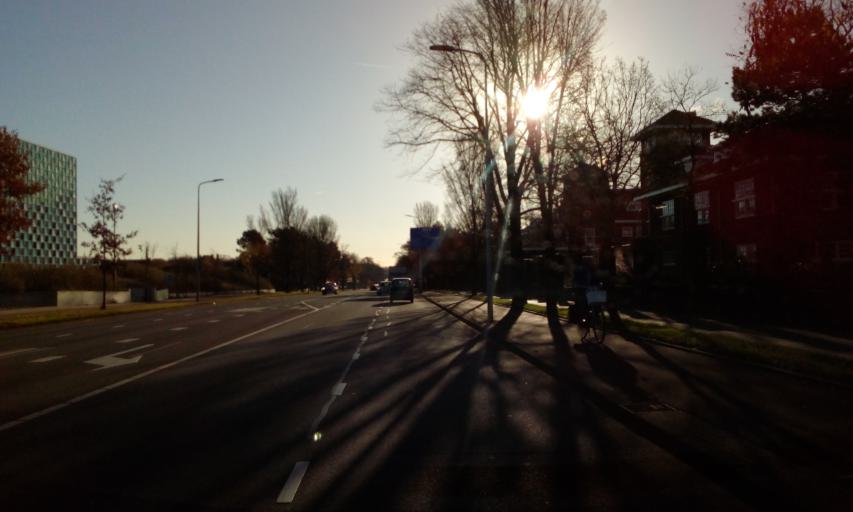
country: NL
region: South Holland
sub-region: Gemeente Den Haag
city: The Hague
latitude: 52.1058
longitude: 4.3151
